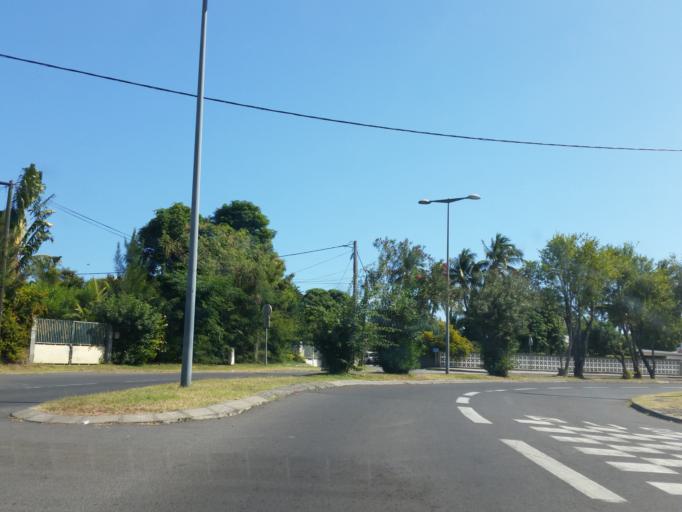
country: RE
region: Reunion
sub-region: Reunion
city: Saint-Paul
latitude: -20.9871
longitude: 55.2886
